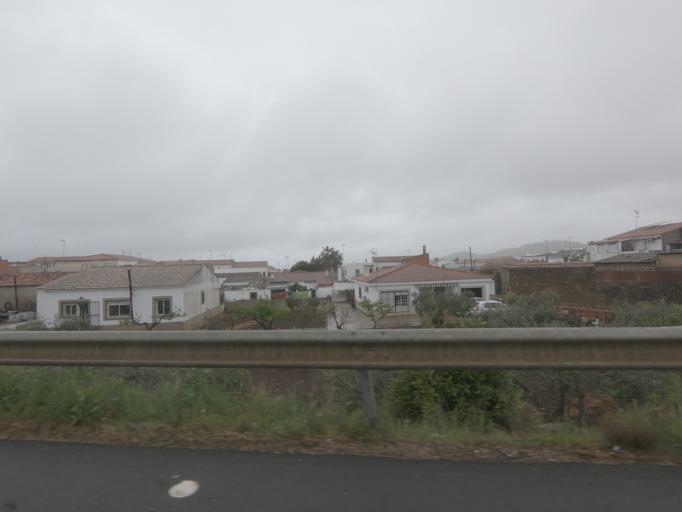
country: ES
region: Extremadura
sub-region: Provincia de Badajoz
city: Puebla de Obando
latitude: 39.1743
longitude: -6.6226
